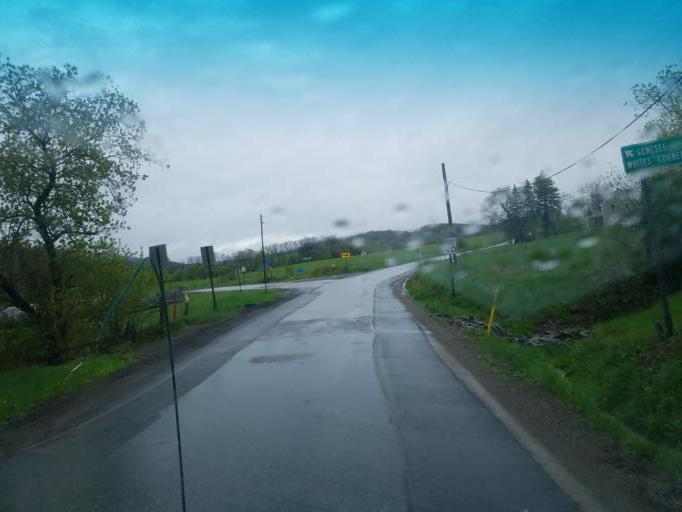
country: US
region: Pennsylvania
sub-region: Tioga County
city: Westfield
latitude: 41.9699
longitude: -77.6600
